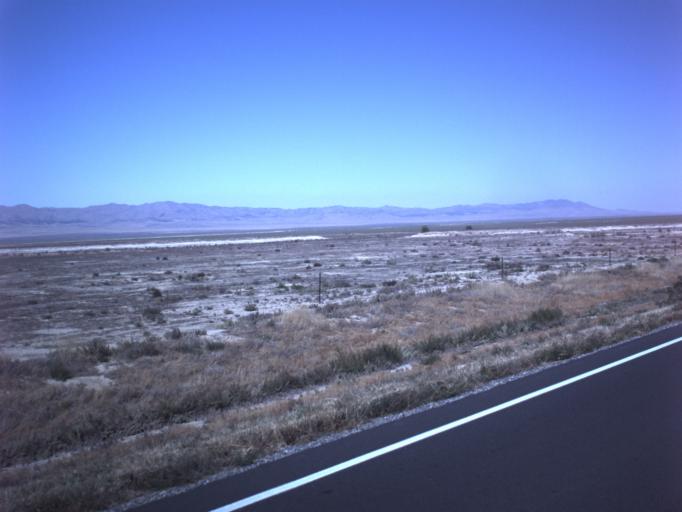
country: US
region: Utah
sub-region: Tooele County
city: Grantsville
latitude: 40.4473
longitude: -112.7485
